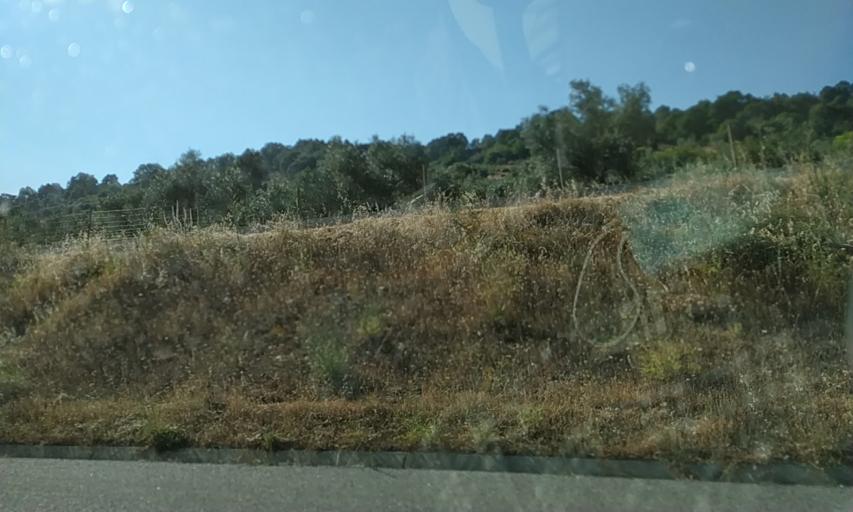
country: PT
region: Braganca
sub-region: Macedo de Cavaleiros
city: Macedo de Cavaleiros
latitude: 41.6168
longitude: -6.8737
